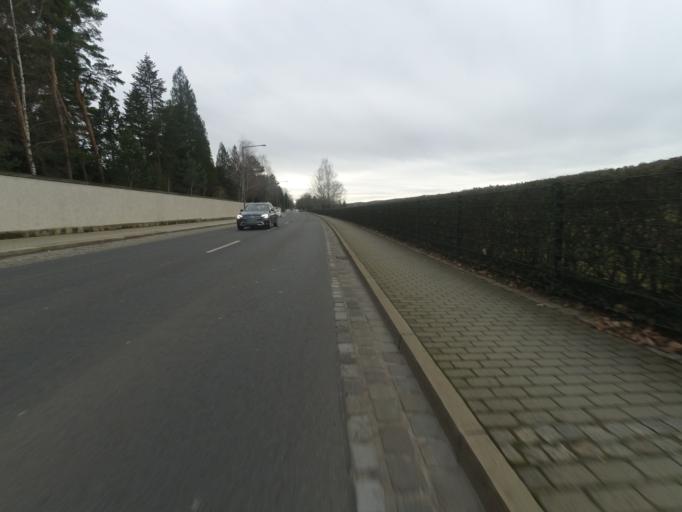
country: DE
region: Saxony
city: Albertstadt
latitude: 51.0361
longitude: 13.8218
